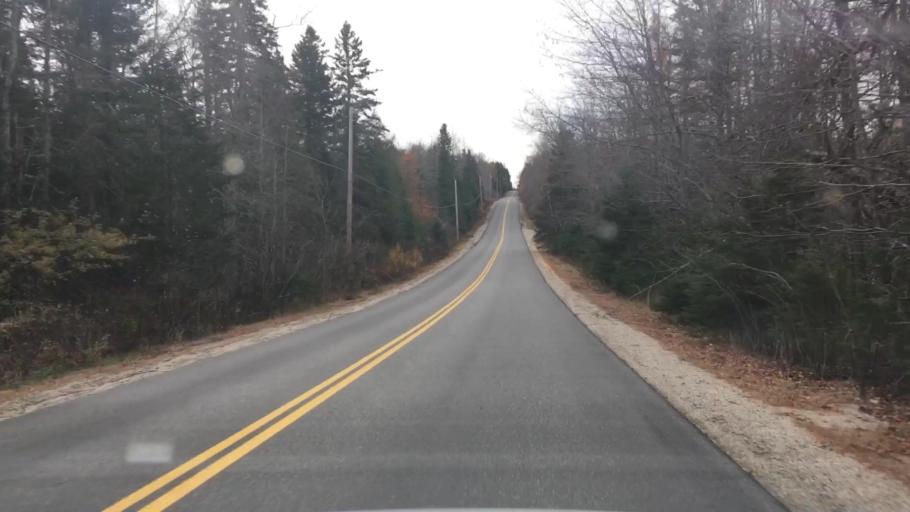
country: US
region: Maine
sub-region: Hancock County
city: Penobscot
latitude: 44.4515
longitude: -68.6372
